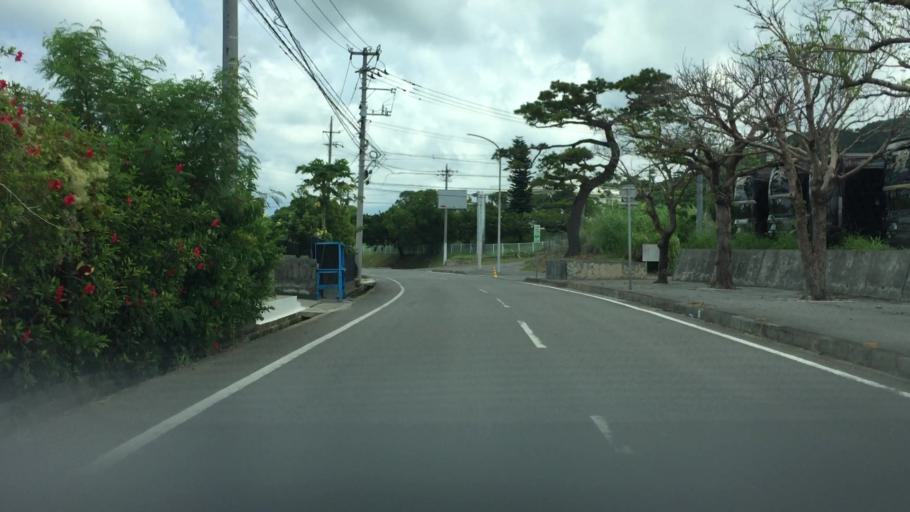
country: JP
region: Okinawa
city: Ishigaki
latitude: 24.3639
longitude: 124.1421
